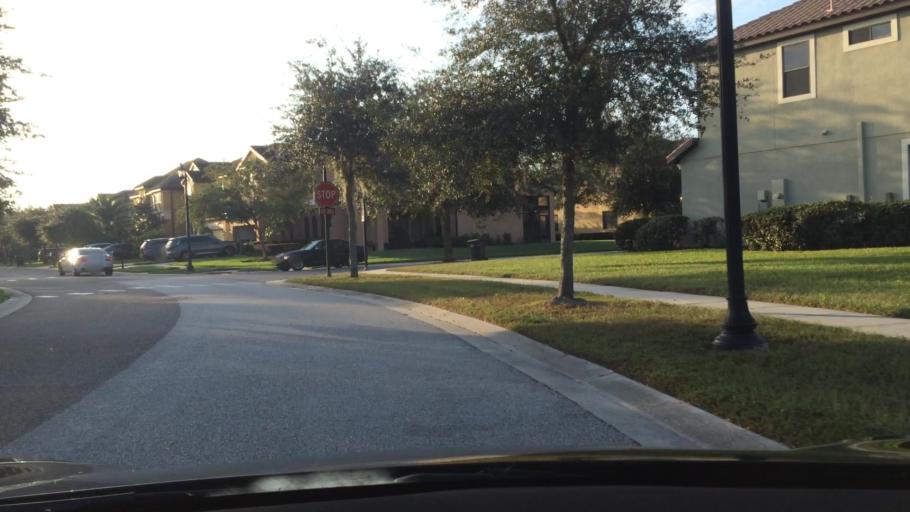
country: US
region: Florida
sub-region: Hillsborough County
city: Pebble Creek
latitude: 28.1686
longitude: -82.3829
